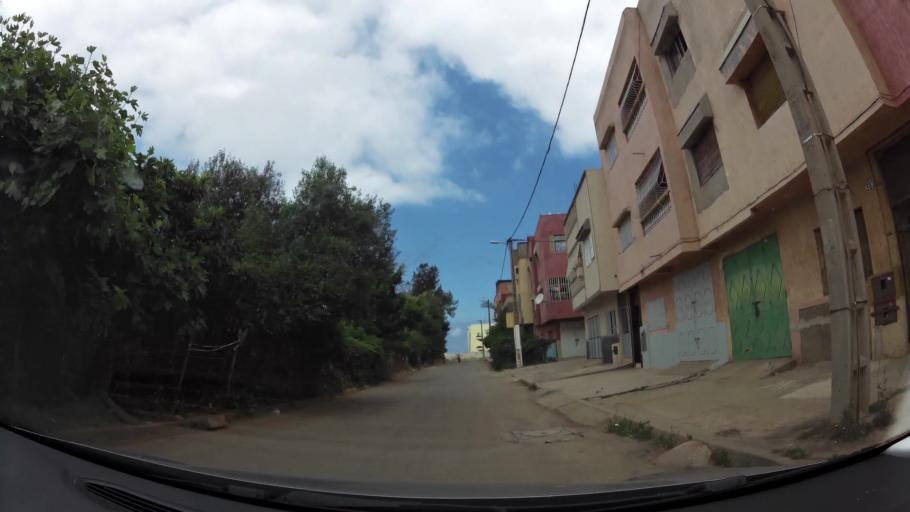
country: MA
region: Rabat-Sale-Zemmour-Zaer
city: Sale
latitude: 34.0631
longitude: -6.7859
